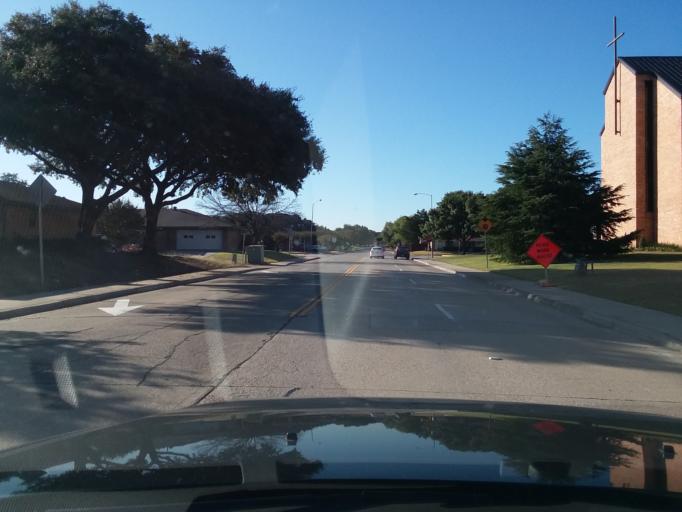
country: US
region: Texas
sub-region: Denton County
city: Lewisville
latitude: 33.0484
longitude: -97.0264
